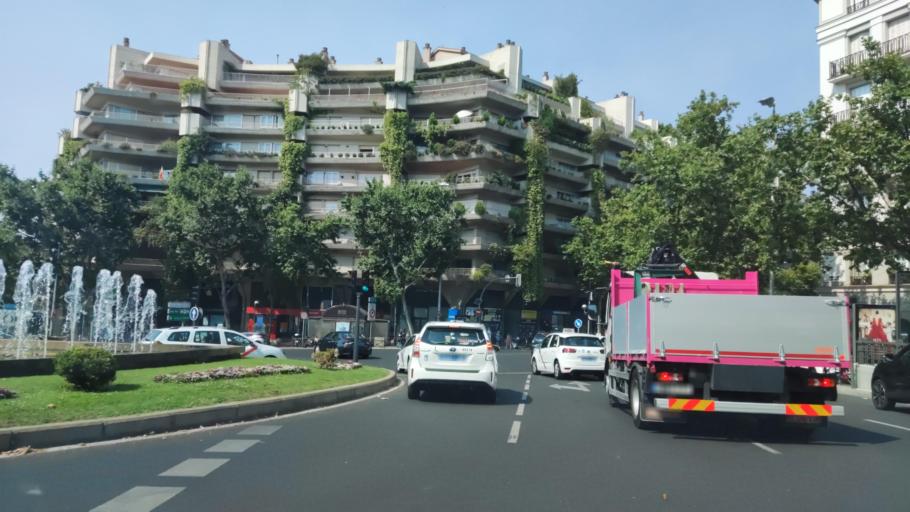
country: ES
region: Madrid
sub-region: Provincia de Madrid
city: Chamberi
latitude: 40.4299
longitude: -3.7058
